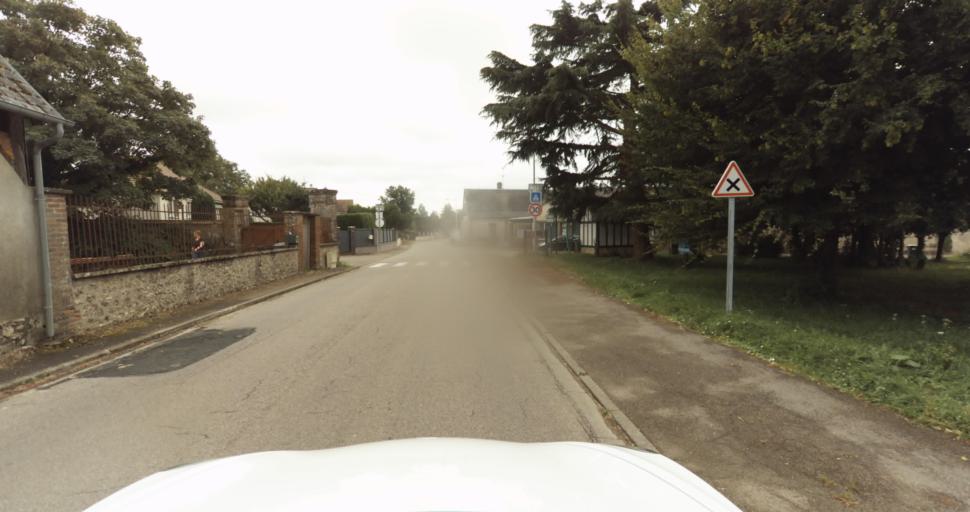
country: FR
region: Haute-Normandie
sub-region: Departement de l'Eure
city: Aviron
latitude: 49.0541
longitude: 1.0865
